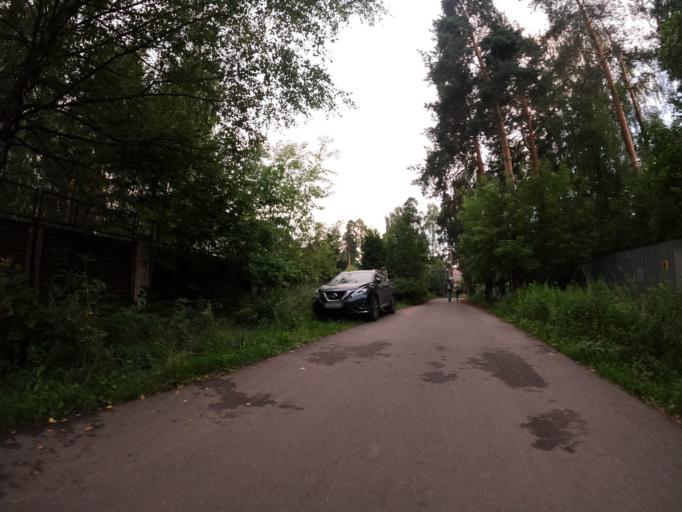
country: RU
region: Moskovskaya
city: Bykovo
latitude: 55.6356
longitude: 38.0681
